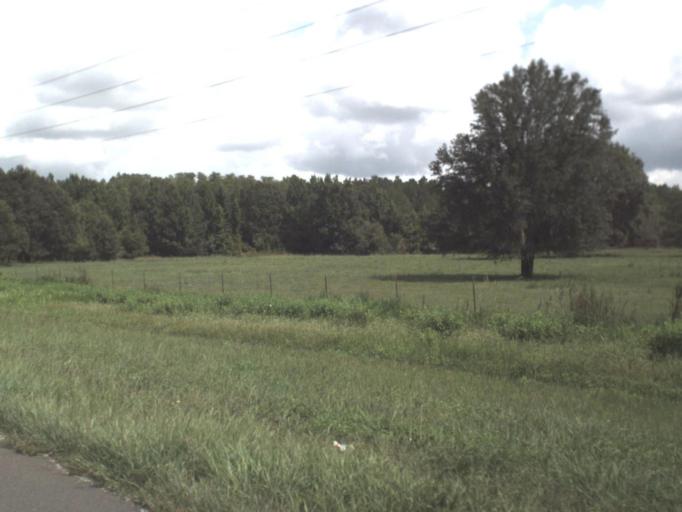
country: US
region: Florida
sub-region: Pasco County
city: Zephyrhills North
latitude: 28.2631
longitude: -82.0825
